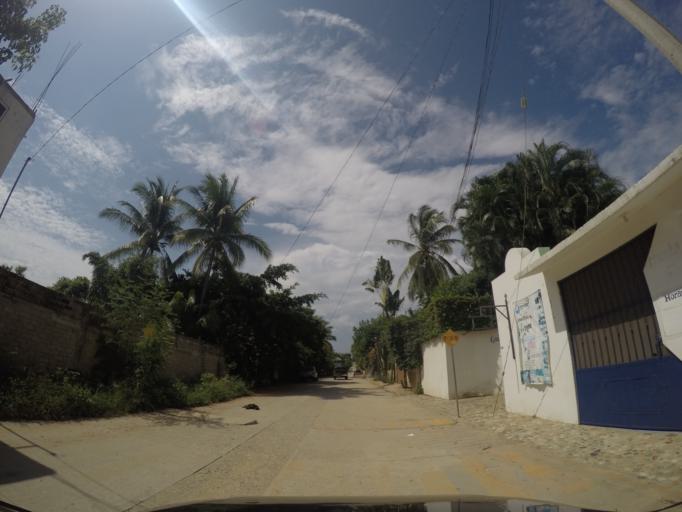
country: MX
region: Oaxaca
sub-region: Santa Maria Colotepec
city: Brisas de Zicatela
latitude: 15.8342
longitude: -97.0424
